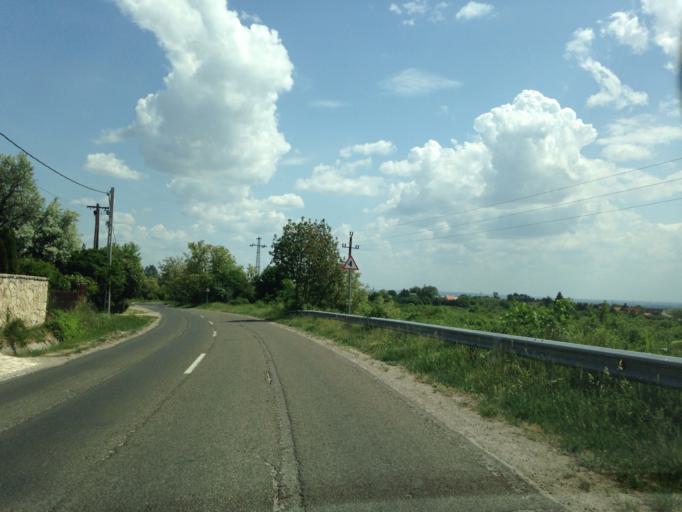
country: HU
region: Pest
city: Szentendre
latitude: 47.6971
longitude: 19.0388
